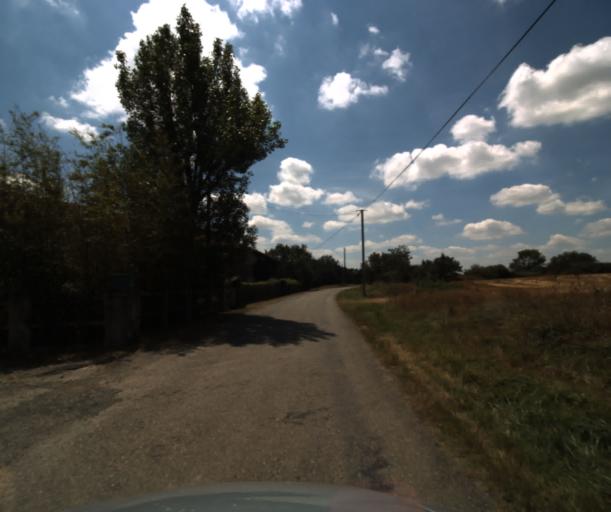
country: FR
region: Midi-Pyrenees
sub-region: Departement de la Haute-Garonne
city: Saint-Lys
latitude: 43.4882
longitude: 1.1902
